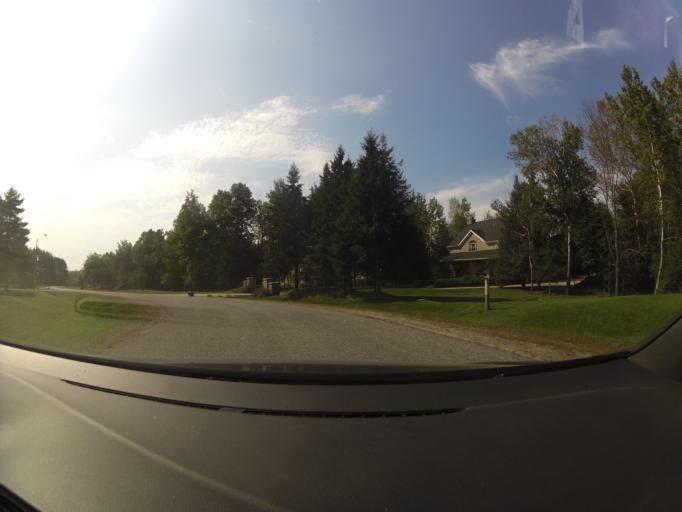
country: CA
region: Ontario
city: Bells Corners
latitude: 45.4437
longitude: -75.9941
